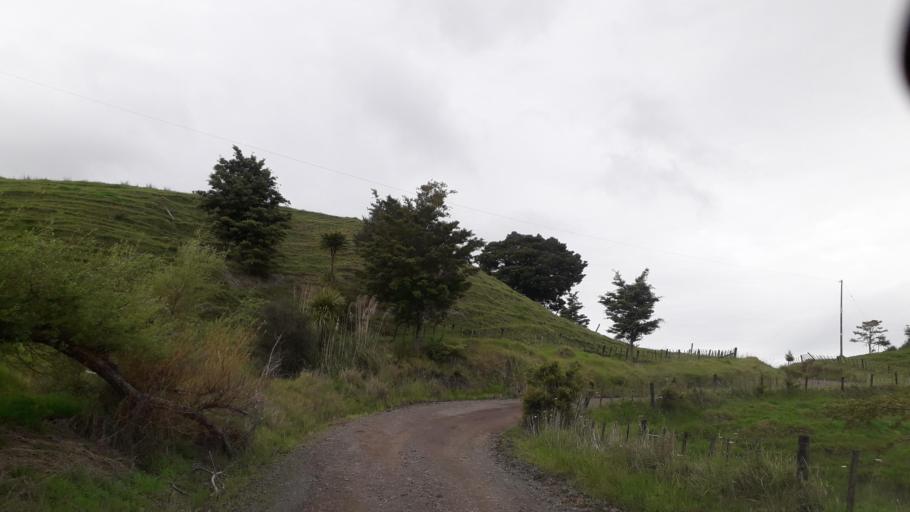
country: NZ
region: Northland
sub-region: Far North District
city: Waimate North
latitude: -35.3114
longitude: 173.5644
